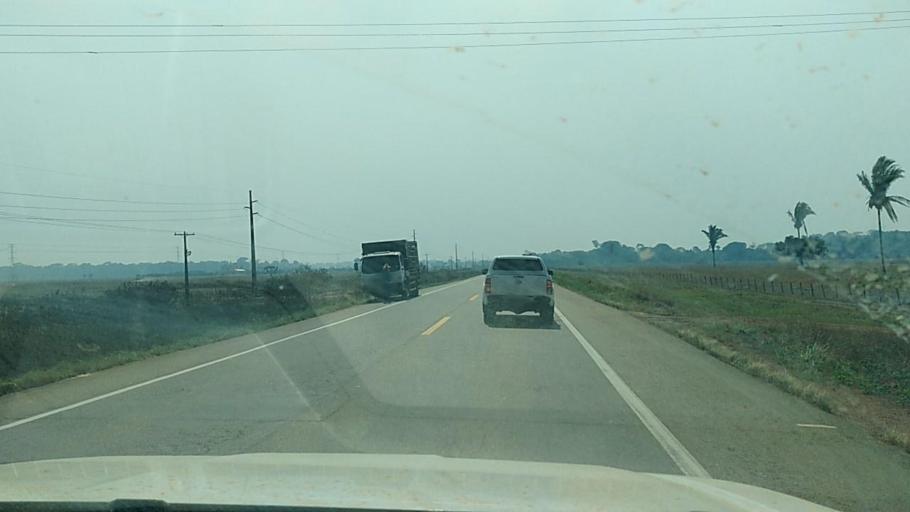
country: BR
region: Rondonia
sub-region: Porto Velho
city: Porto Velho
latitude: -8.7822
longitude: -63.5565
